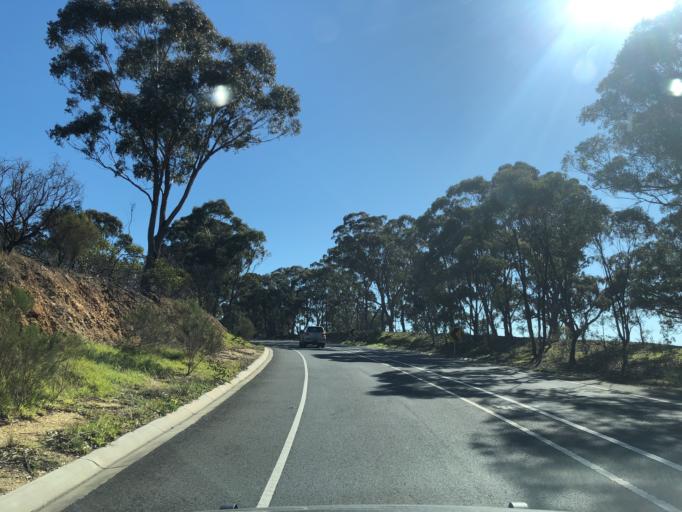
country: AU
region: Victoria
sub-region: Melton
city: Melton West
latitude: -37.6145
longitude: 144.5248
